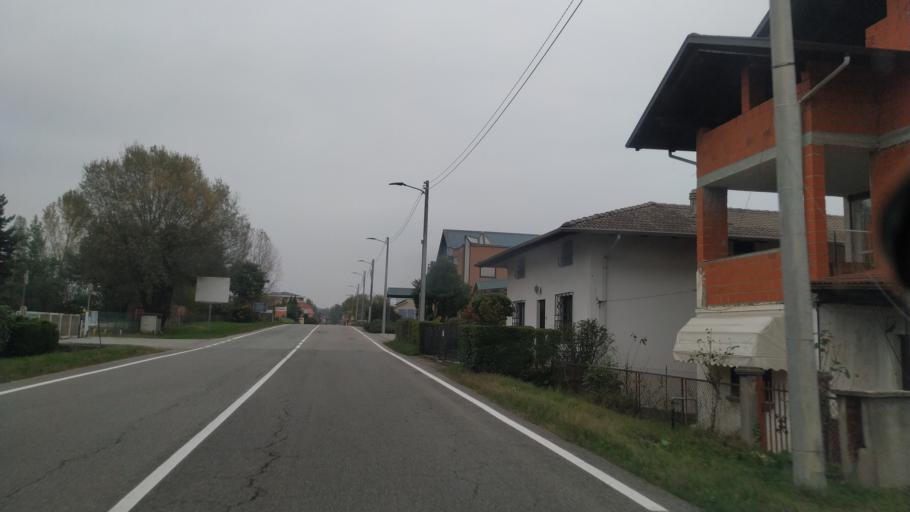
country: IT
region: Piedmont
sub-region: Provincia di Biella
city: Cerreto Castello
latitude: 45.5604
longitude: 8.1735
